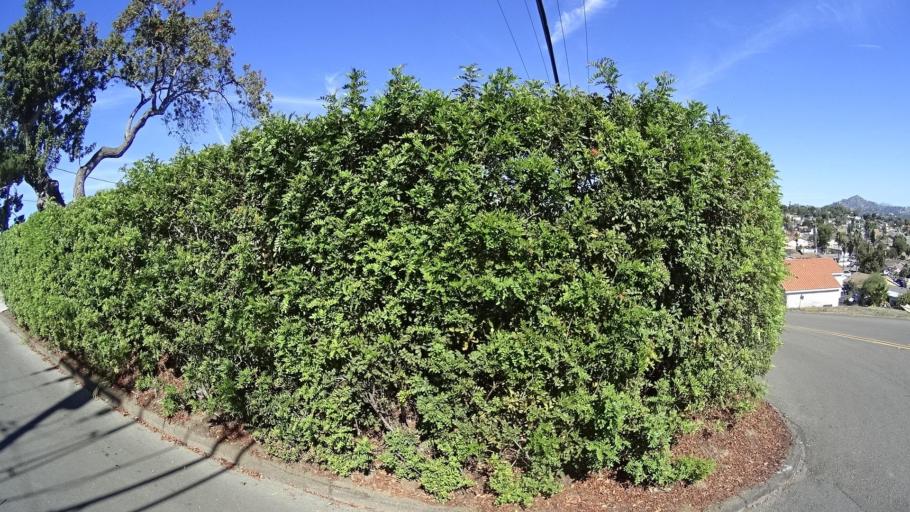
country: US
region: California
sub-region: San Diego County
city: Lemon Grove
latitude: 32.7234
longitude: -117.0232
